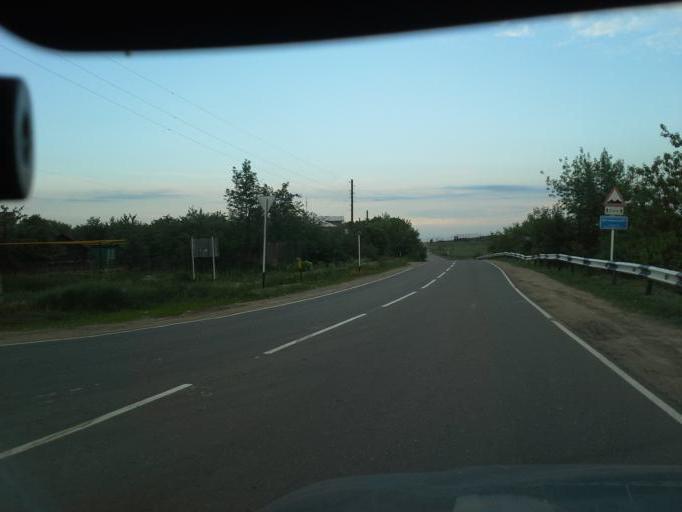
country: RU
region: Ivanovo
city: Gavrilov Posad
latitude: 56.5592
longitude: 40.1369
